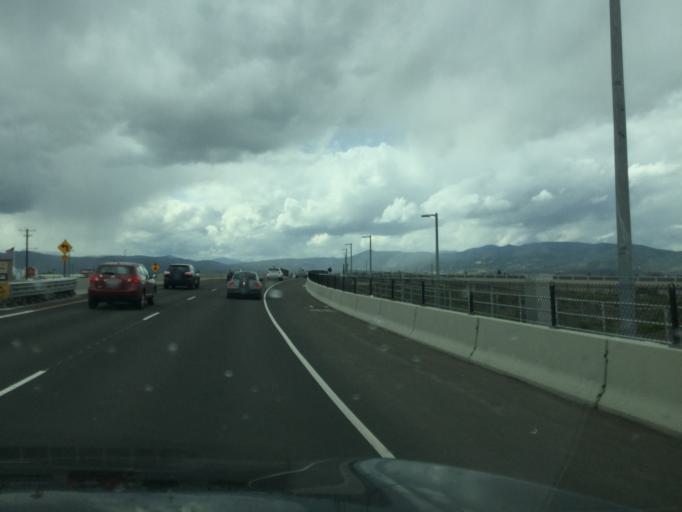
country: US
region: Oregon
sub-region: Jackson County
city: Medford
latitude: 42.3597
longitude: -122.8611
